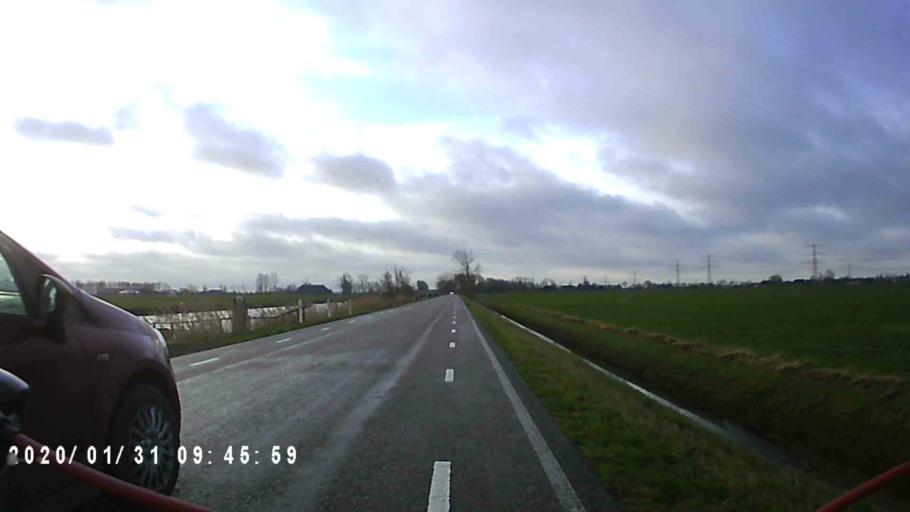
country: NL
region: Groningen
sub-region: Gemeente Zuidhorn
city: Aduard
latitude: 53.2675
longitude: 6.4833
